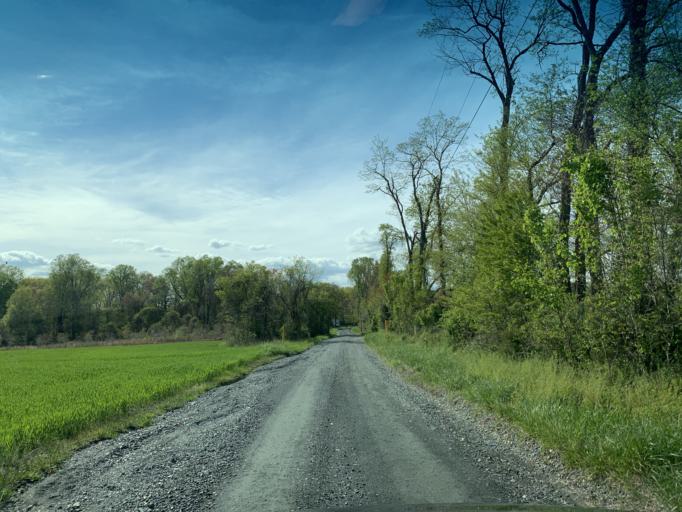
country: US
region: Maryland
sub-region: Harford County
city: Perryman
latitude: 39.4713
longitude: -76.2162
